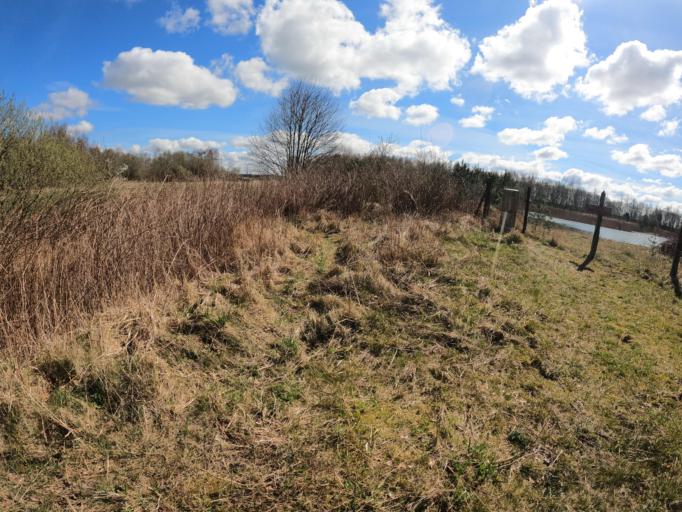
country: PL
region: West Pomeranian Voivodeship
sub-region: Powiat gryficki
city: Gryfice
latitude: 53.9241
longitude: 15.2323
